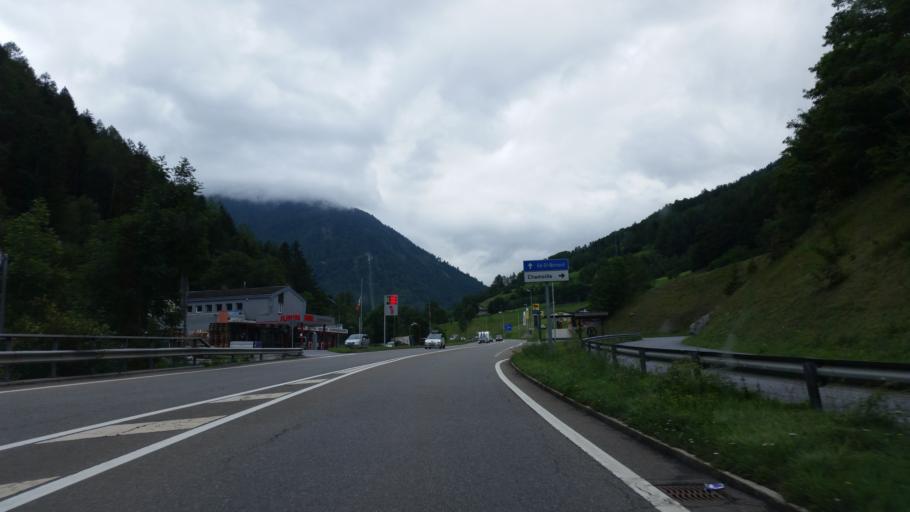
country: CH
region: Valais
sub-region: Entremont District
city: Orsieres
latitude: 46.0432
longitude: 7.1485
